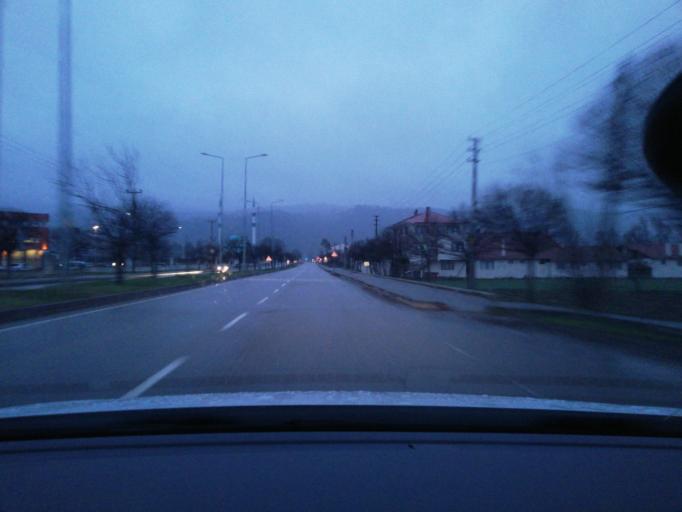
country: TR
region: Bolu
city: Bolu
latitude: 40.6930
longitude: 31.6195
